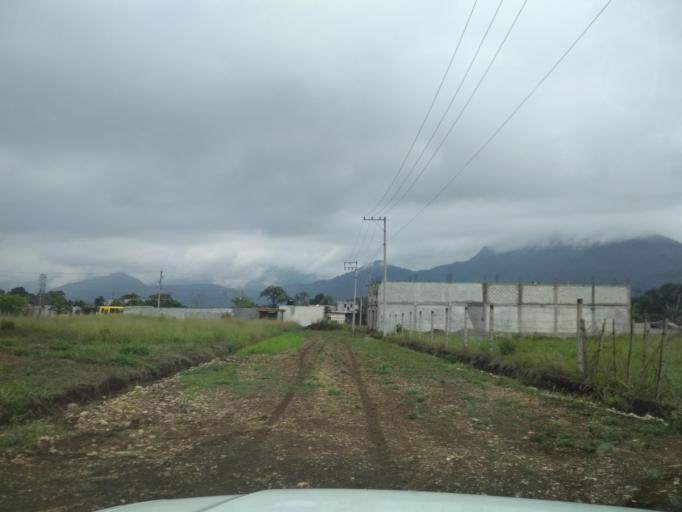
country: MX
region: Veracruz
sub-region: Cordoba
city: San Jose de Tapia
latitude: 18.8434
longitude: -96.9683
